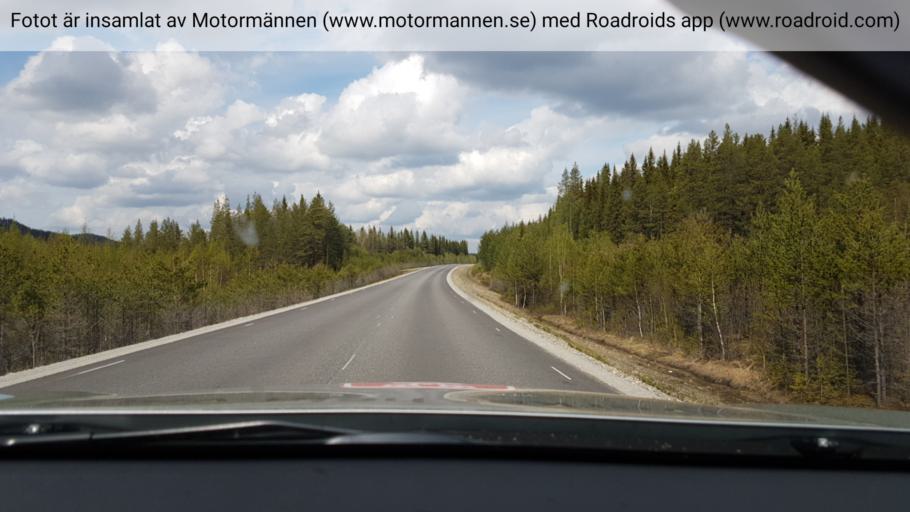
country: SE
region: Vaesterbotten
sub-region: Lycksele Kommun
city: Lycksele
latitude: 64.0015
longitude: 18.4659
